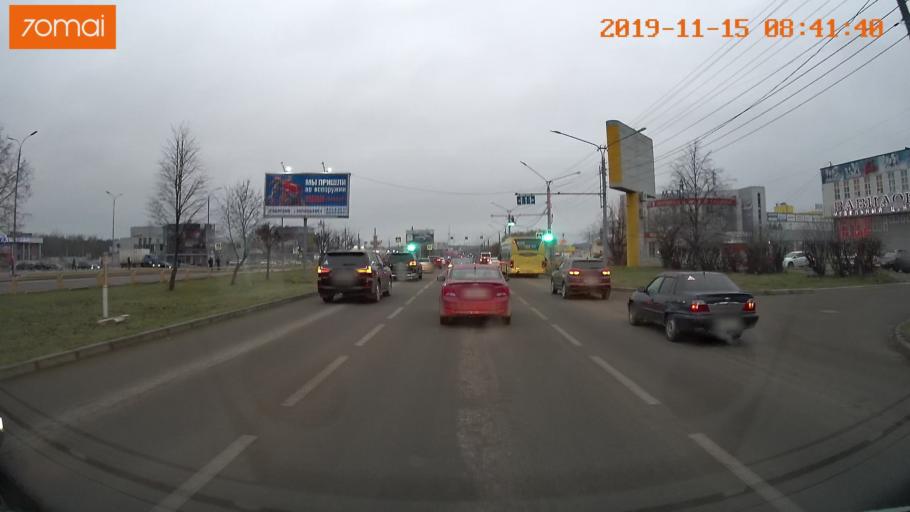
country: RU
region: Vologda
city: Cherepovets
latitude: 59.0977
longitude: 37.9117
